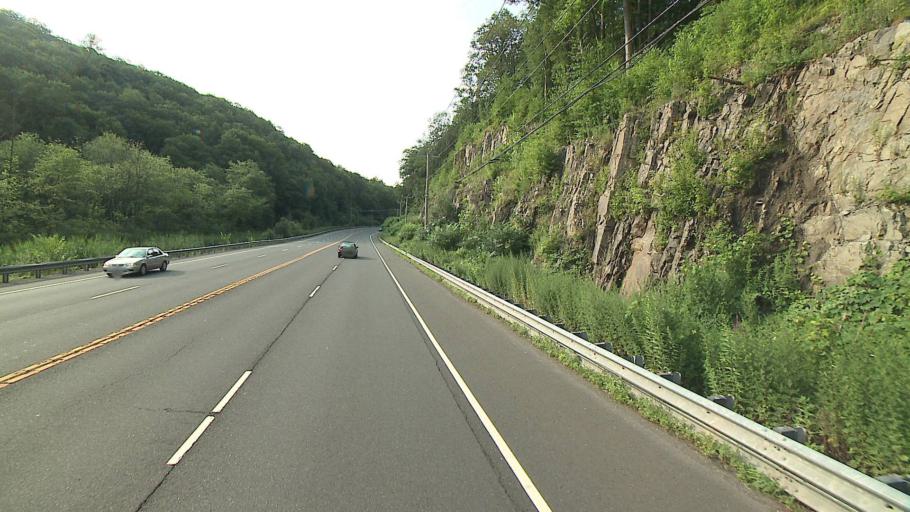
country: US
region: Connecticut
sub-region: Fairfield County
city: Danbury
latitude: 41.3567
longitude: -73.4712
